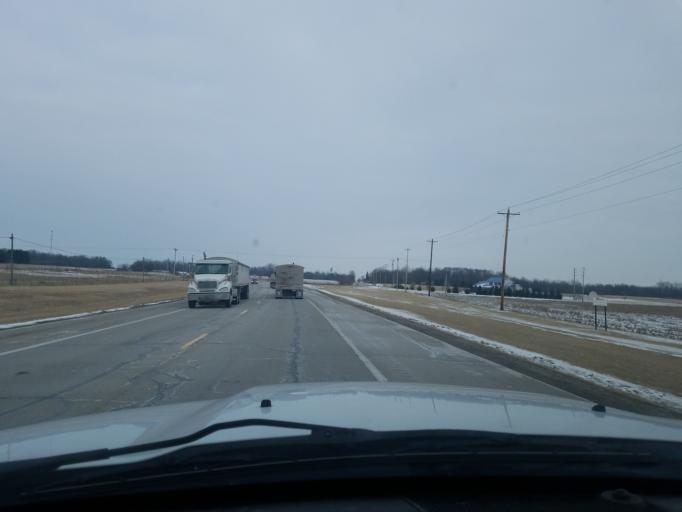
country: US
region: Indiana
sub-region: Randolph County
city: Lynn
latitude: 40.0486
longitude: -84.9612
